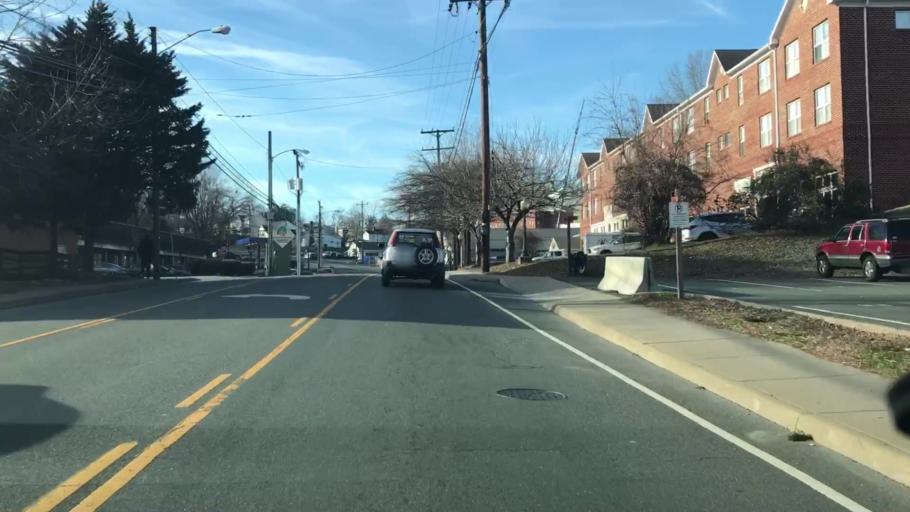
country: US
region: Virginia
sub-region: City of Charlottesville
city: Charlottesville
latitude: 38.0285
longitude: -78.4931
